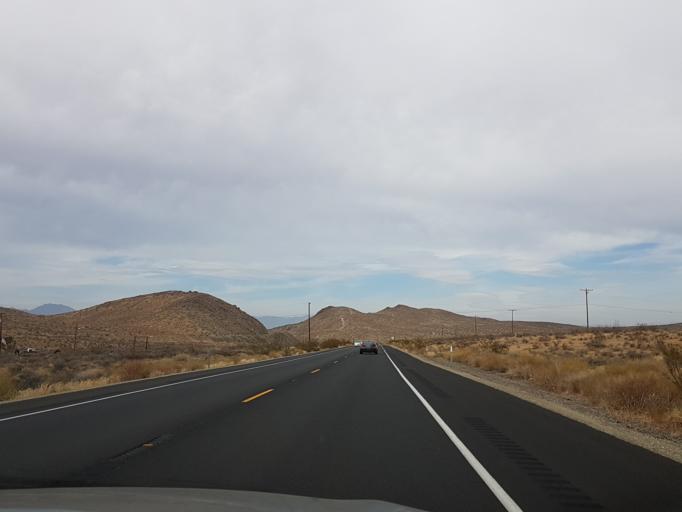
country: US
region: California
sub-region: Kern County
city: Ridgecrest
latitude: 35.5370
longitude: -117.6844
